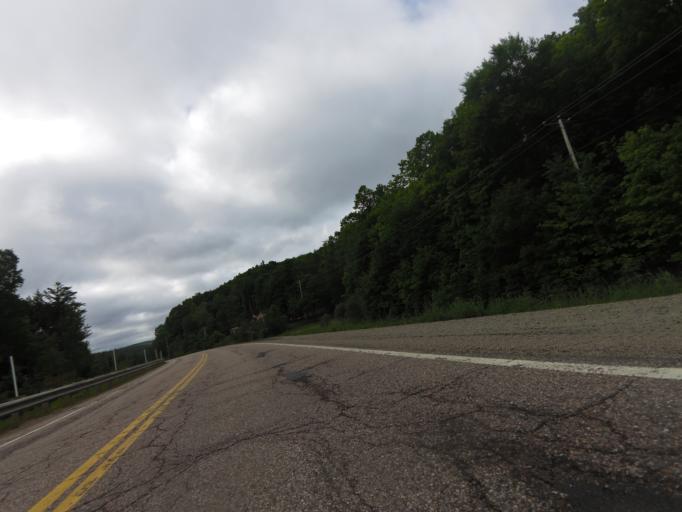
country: CA
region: Quebec
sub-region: Outaouais
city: Shawville
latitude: 45.8320
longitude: -76.4617
